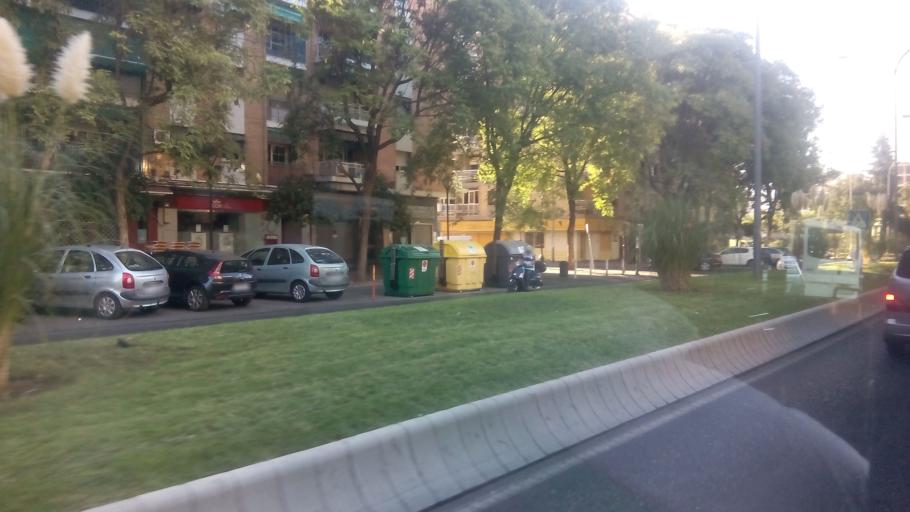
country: ES
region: Andalusia
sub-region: Province of Cordoba
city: Cordoba
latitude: 37.8882
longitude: -4.7642
